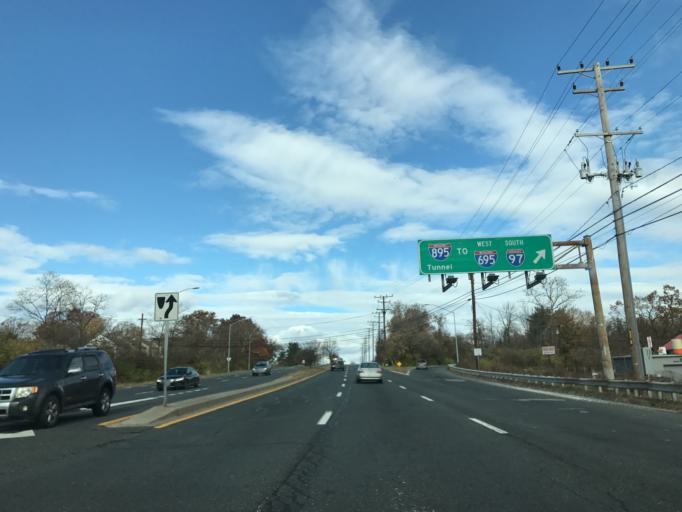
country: US
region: Maryland
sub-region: Anne Arundel County
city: Brooklyn Park
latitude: 39.1982
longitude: -76.6133
